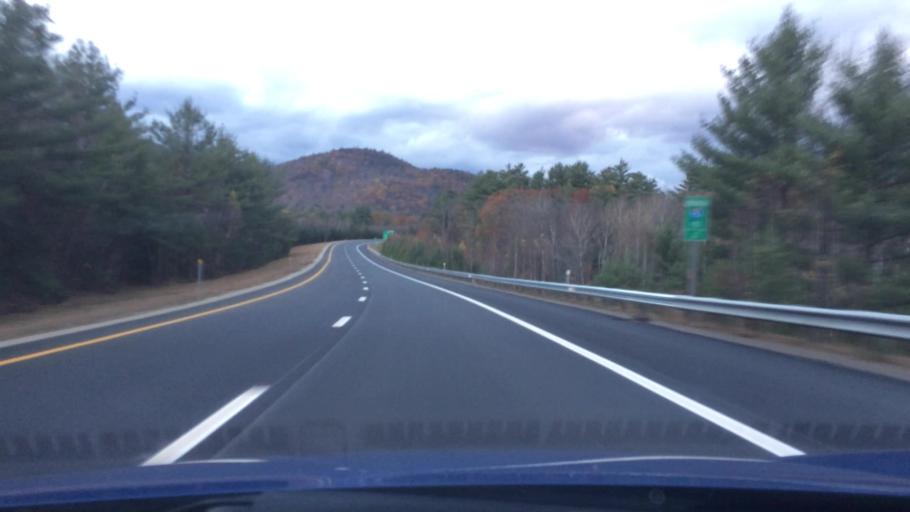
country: US
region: New Hampshire
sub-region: Grafton County
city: Thornton
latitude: 43.9325
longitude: -71.6866
